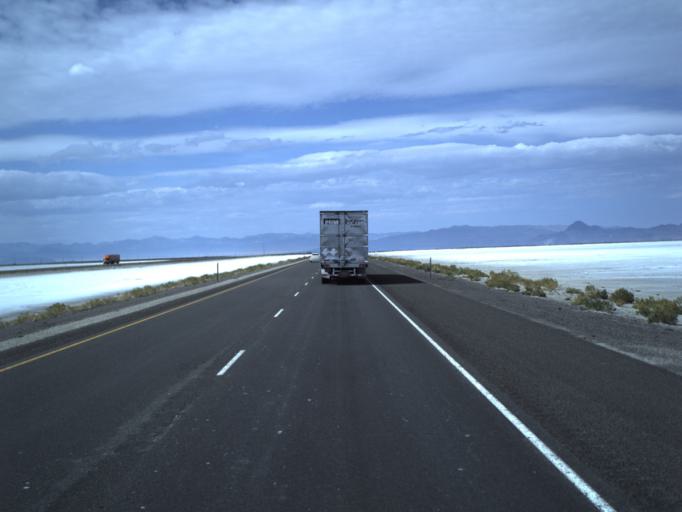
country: US
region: Utah
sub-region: Tooele County
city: Wendover
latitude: 40.7366
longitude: -113.7158
